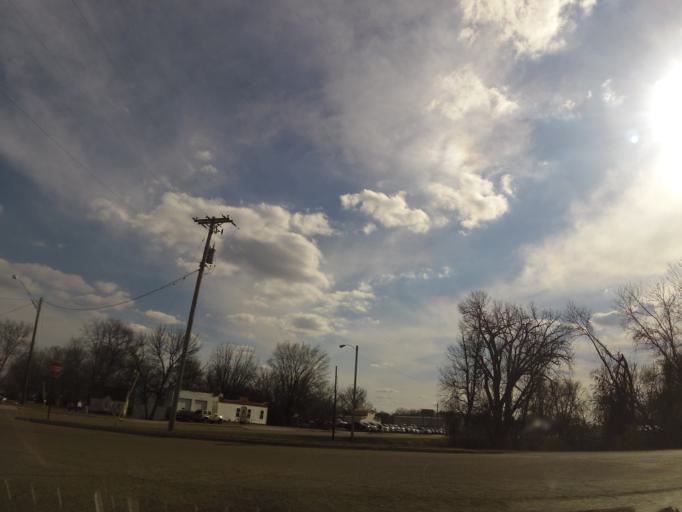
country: US
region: Minnesota
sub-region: Chippewa County
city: Montevideo
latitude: 44.9390
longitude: -95.7244
